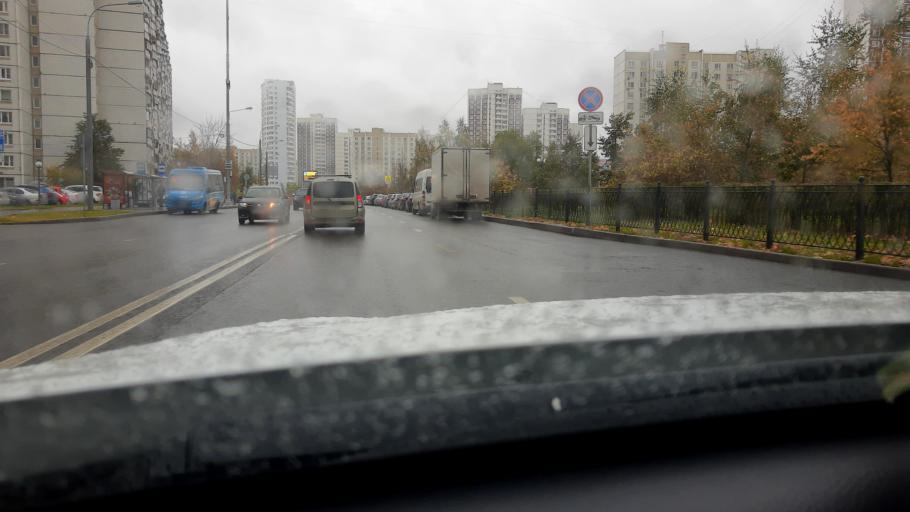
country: RU
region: Moskovskaya
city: Pavshino
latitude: 55.8523
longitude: 37.3536
